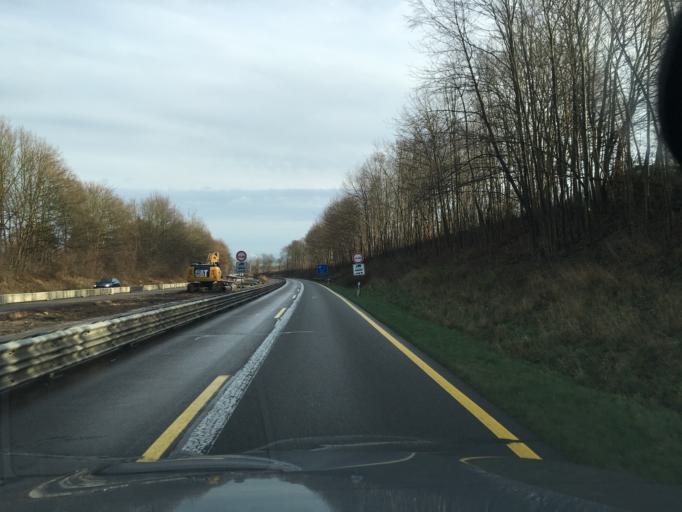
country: DE
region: North Rhine-Westphalia
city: Bruhl
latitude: 50.7979
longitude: 6.8905
